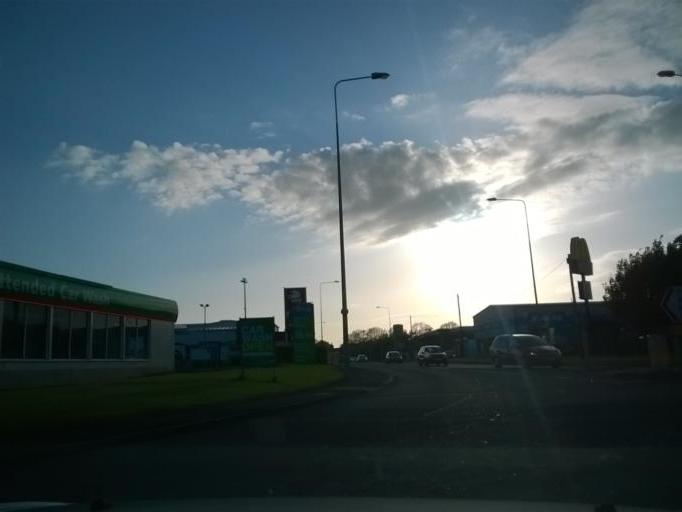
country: GB
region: Wales
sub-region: Bridgend county borough
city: Bridgend
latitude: 51.4952
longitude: -3.5666
